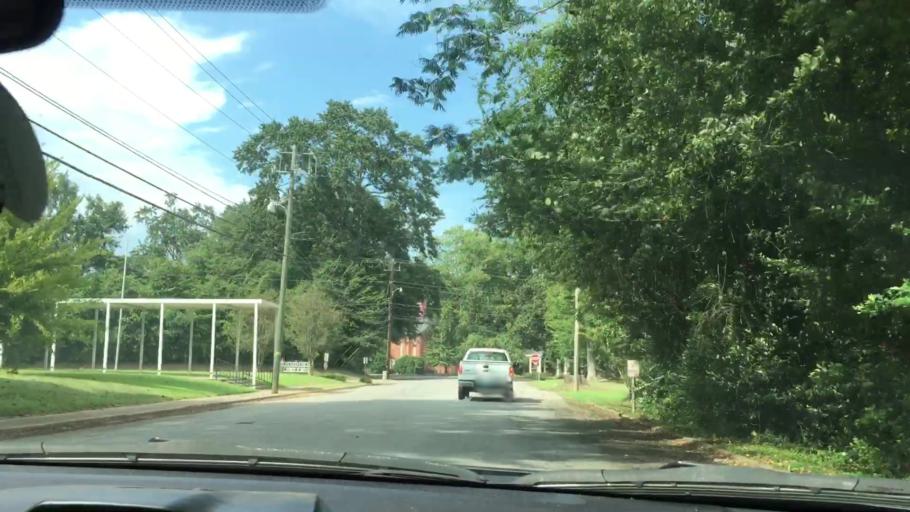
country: US
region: Alabama
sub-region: Hale County
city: Greensboro
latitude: 32.7022
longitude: -87.5989
